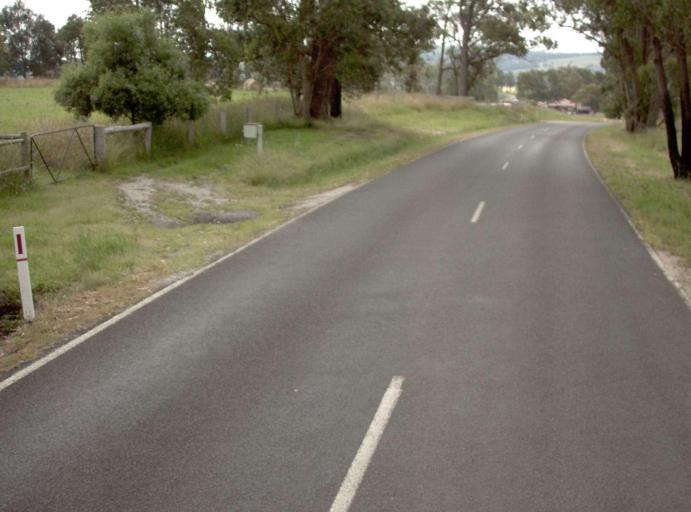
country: AU
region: Victoria
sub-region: Latrobe
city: Traralgon
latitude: -38.3831
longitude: 146.7963
